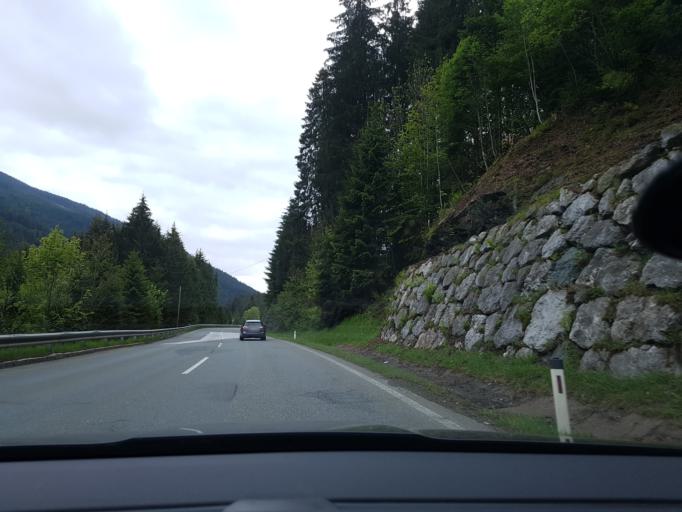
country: AT
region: Tyrol
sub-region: Politischer Bezirk Kitzbuhel
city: Jochberg
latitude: 47.3526
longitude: 12.4137
